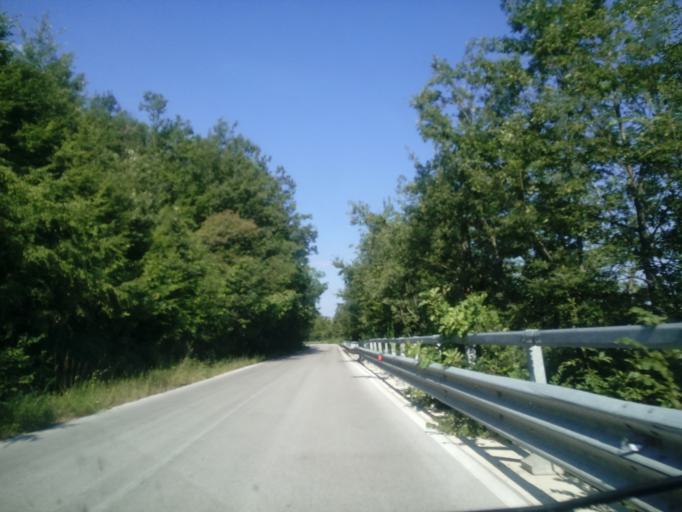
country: IT
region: Molise
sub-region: Provincia di Campobasso
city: Gildone
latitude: 41.5150
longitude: 14.7480
